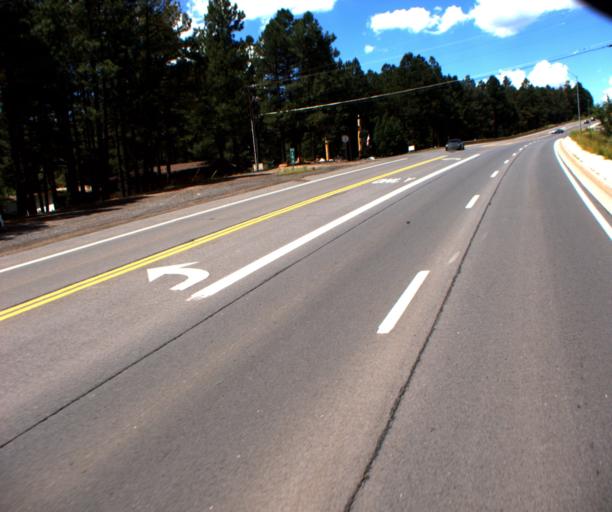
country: US
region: Arizona
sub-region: Coconino County
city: Flagstaff
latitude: 35.1878
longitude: -111.6831
